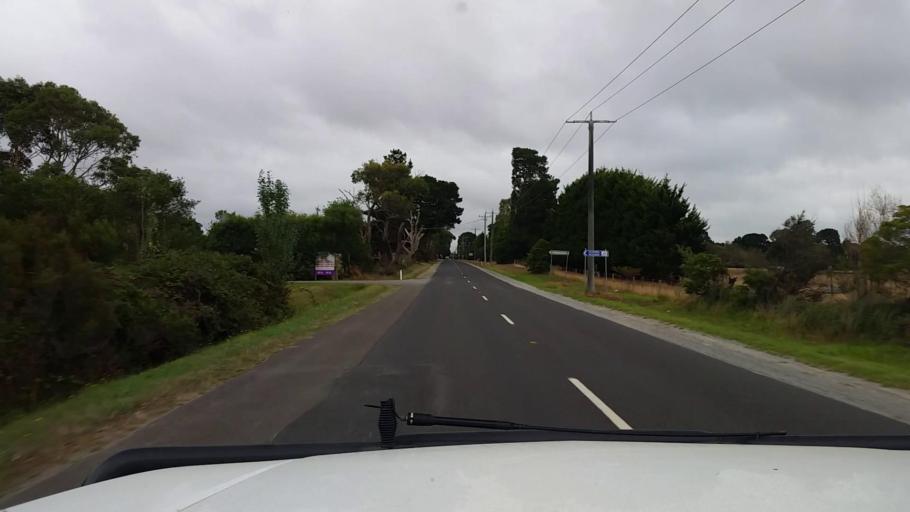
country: AU
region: Victoria
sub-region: Mornington Peninsula
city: Balnarring
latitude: -38.3431
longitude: 145.1457
